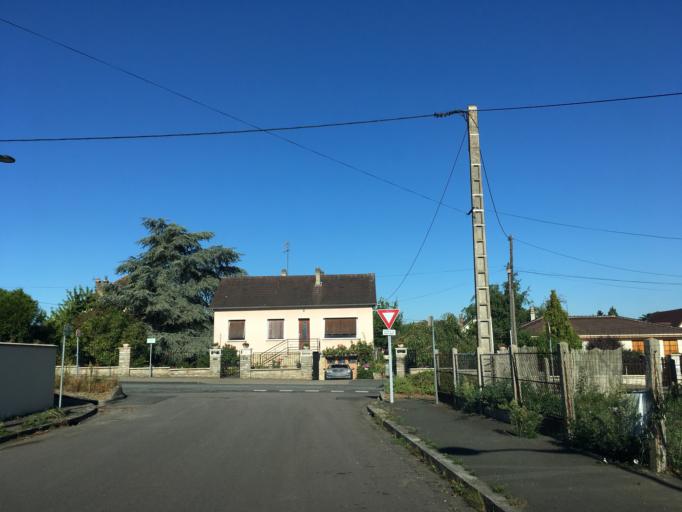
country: FR
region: Haute-Normandie
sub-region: Departement de l'Eure
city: Vernon
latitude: 49.0828
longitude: 1.4859
